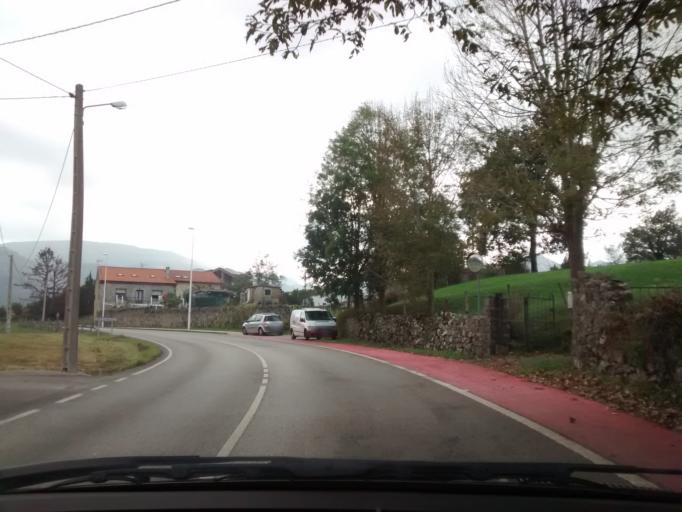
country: ES
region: Cantabria
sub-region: Provincia de Cantabria
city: Entrambasaguas
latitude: 43.3559
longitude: -3.7036
